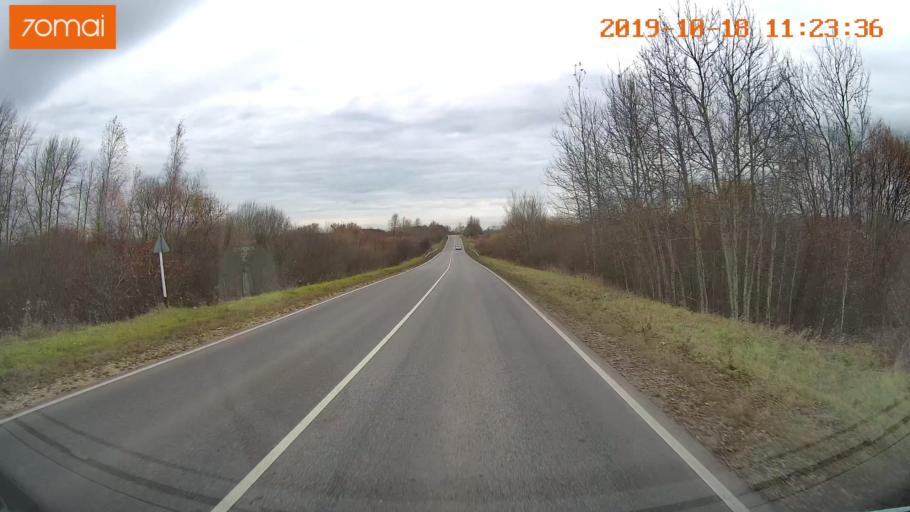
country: RU
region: Tula
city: Kimovsk
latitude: 54.1036
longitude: 38.5949
